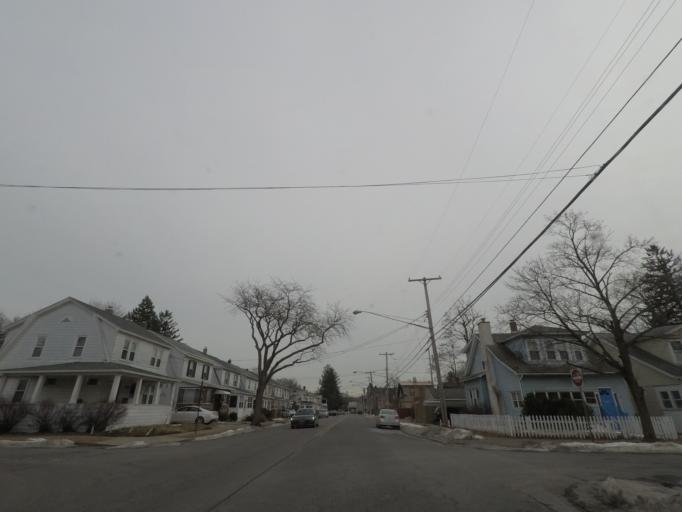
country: US
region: New York
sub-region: Albany County
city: West Albany
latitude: 42.6739
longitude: -73.7886
